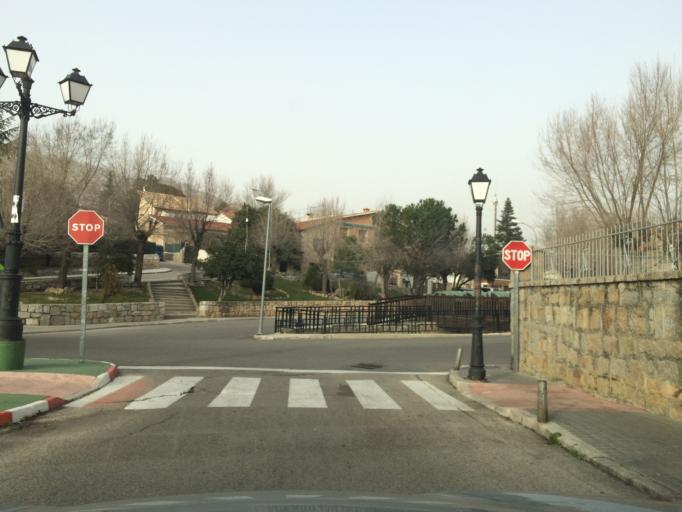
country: ES
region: Madrid
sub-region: Provincia de Madrid
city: Manzanares el Real
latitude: 40.7293
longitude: -3.8651
